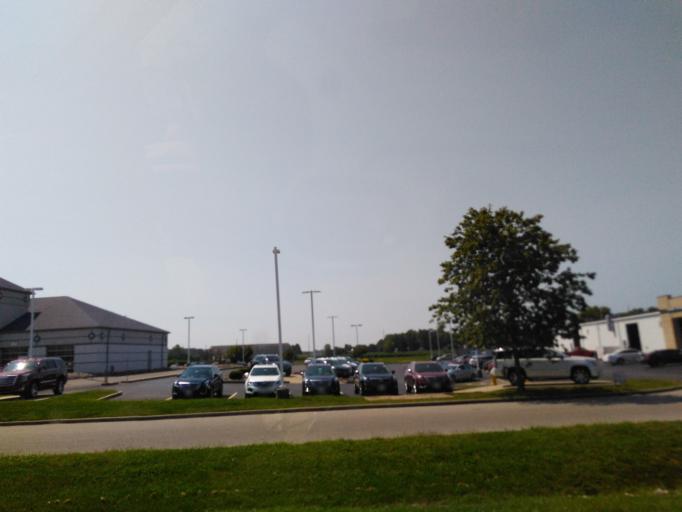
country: US
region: Illinois
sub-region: Saint Clair County
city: O'Fallon
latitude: 38.5924
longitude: -89.9353
